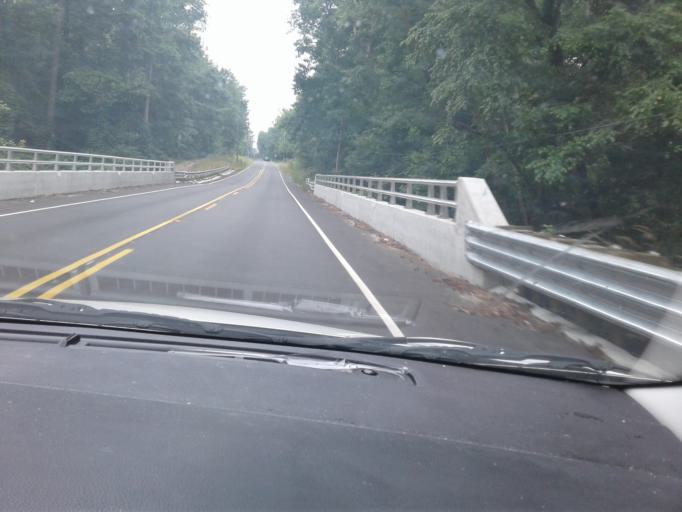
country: US
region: North Carolina
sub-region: Harnett County
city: Buies Creek
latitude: 35.4118
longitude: -78.7278
